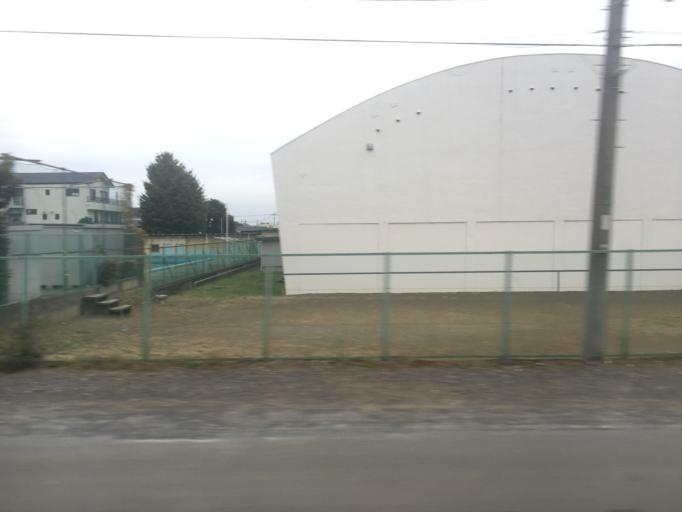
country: JP
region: Saitama
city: Hanno
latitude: 35.8581
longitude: 139.3262
